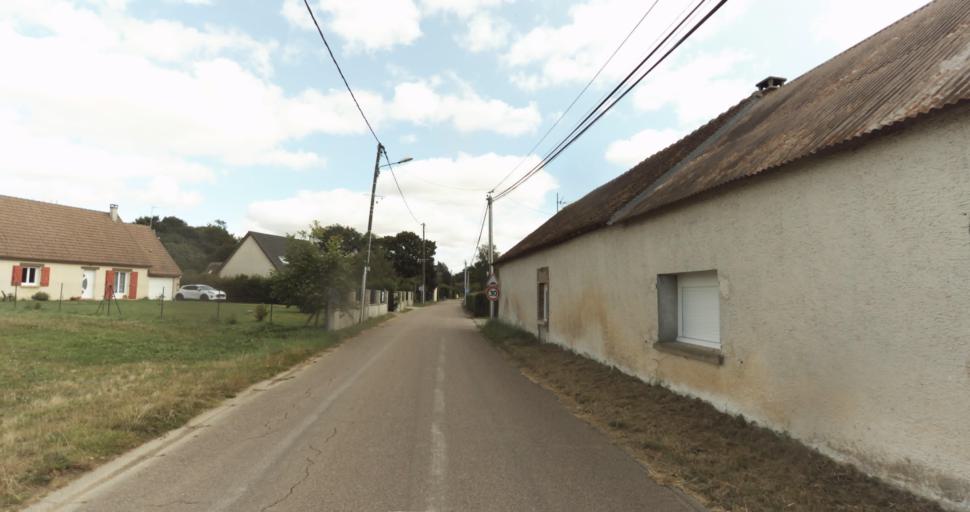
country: FR
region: Haute-Normandie
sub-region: Departement de l'Eure
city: Nonancourt
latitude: 48.8334
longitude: 1.1705
